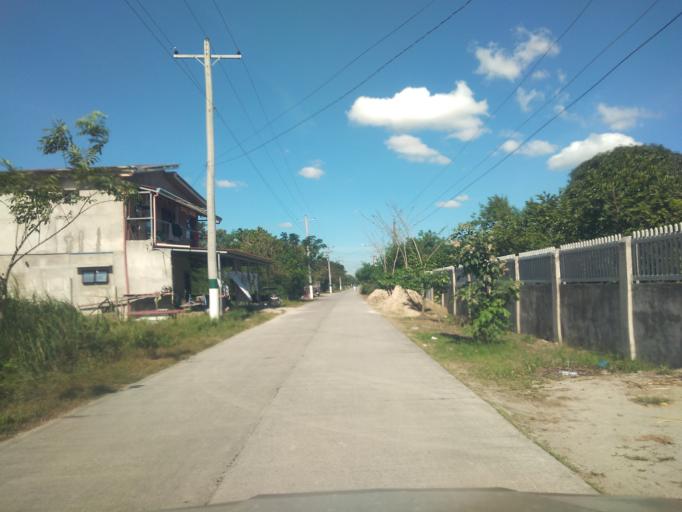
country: PH
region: Central Luzon
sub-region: Province of Pampanga
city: Bacolor
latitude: 15.0106
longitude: 120.6366
